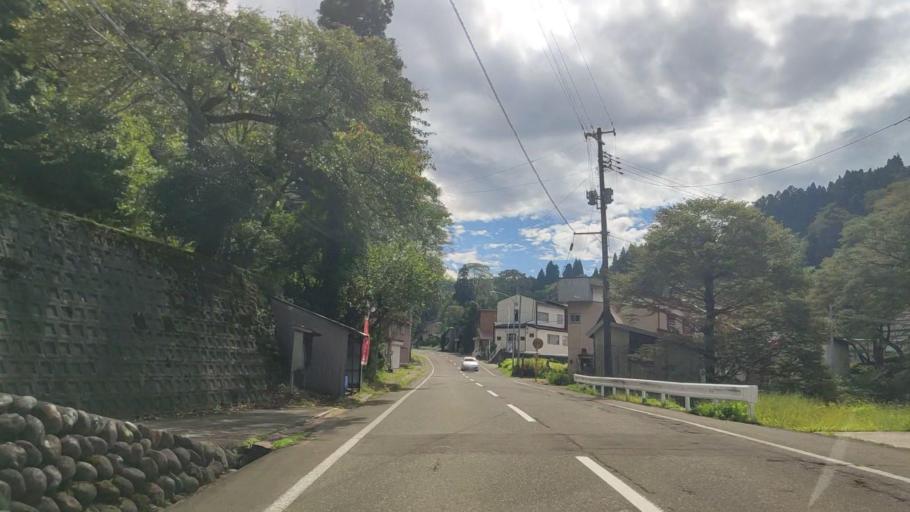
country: JP
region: Niigata
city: Arai
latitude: 36.9289
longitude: 138.2986
